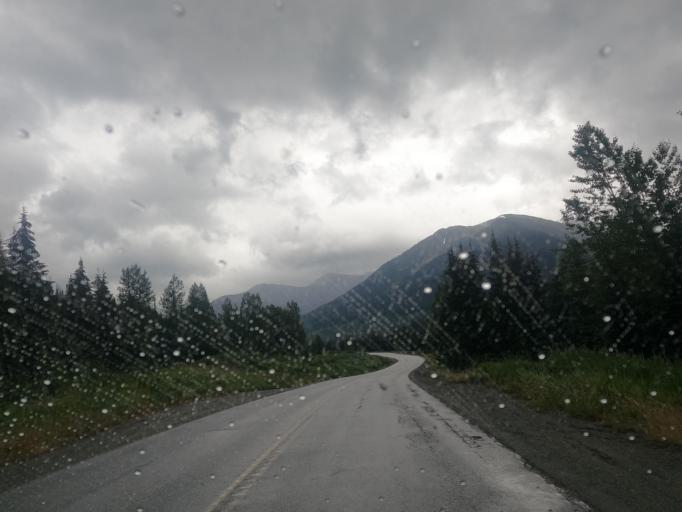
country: CA
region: British Columbia
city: Pemberton
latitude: 50.3838
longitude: -122.4258
